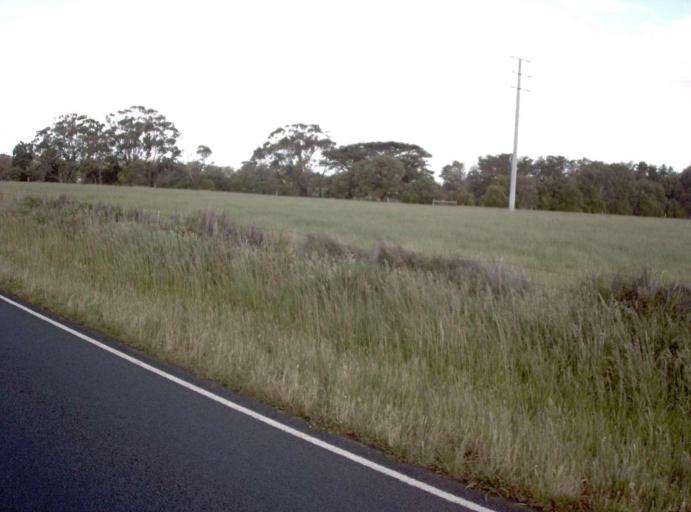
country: AU
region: Victoria
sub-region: Bass Coast
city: North Wonthaggi
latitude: -38.5313
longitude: 145.8779
